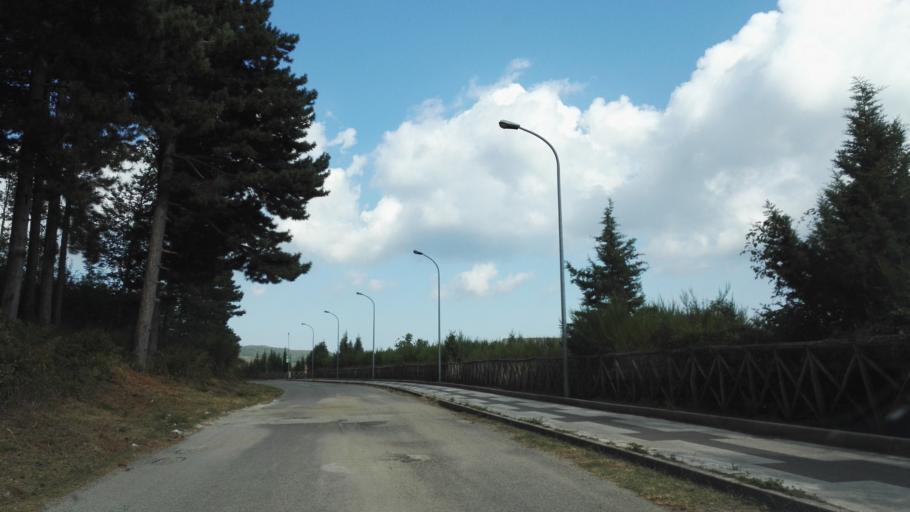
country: IT
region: Calabria
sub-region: Provincia di Vibo-Valentia
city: Nardodipace
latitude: 38.4769
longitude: 16.3424
